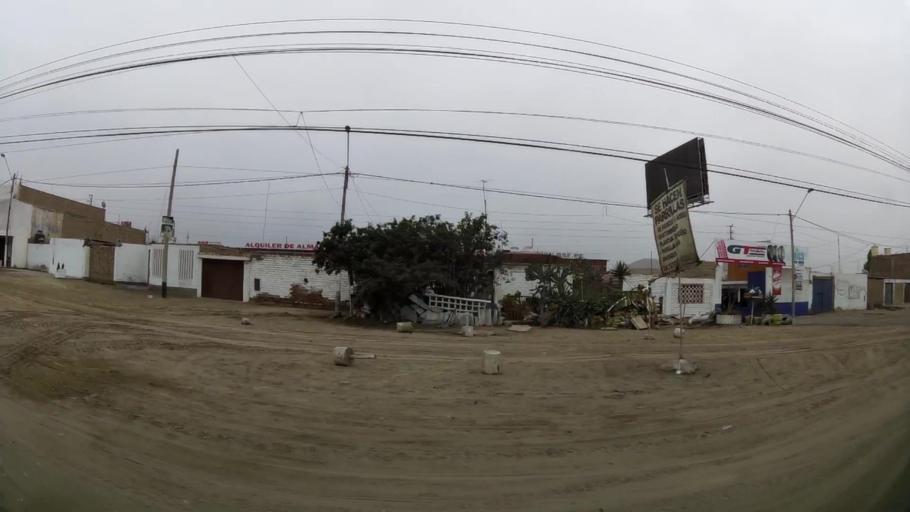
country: PE
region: Lima
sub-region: Lima
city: Punta Hermosa
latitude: -12.3210
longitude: -76.8293
